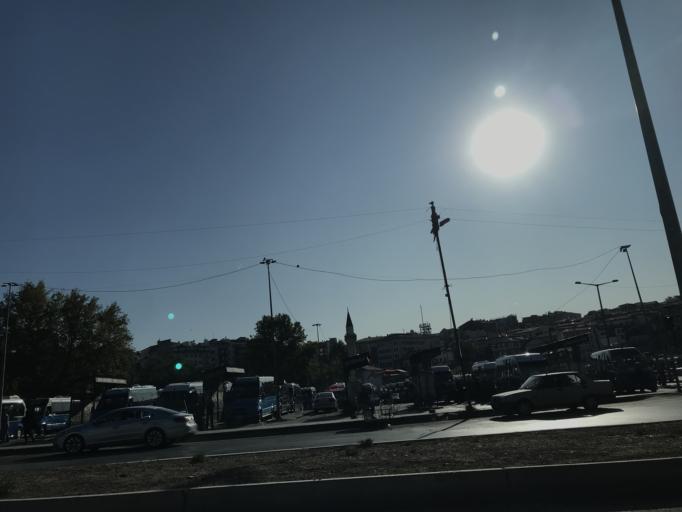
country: TR
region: Ankara
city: Ankara
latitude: 39.9434
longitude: 32.8617
